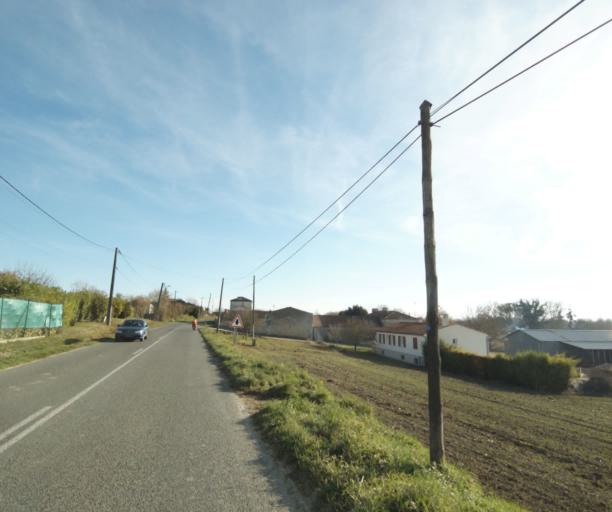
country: FR
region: Poitou-Charentes
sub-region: Departement de la Charente-Maritime
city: Chaniers
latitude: 45.7251
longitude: -0.5736
